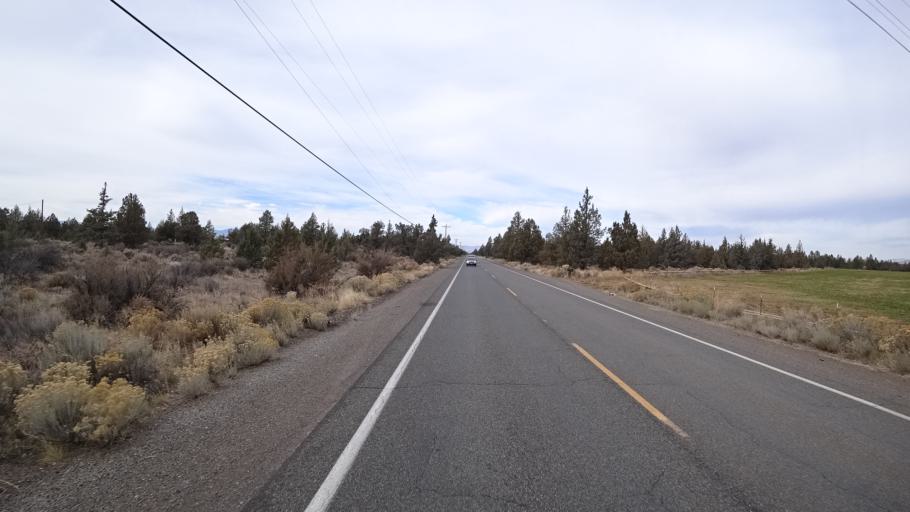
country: US
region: California
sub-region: Siskiyou County
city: Weed
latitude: 41.5991
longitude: -122.3453
